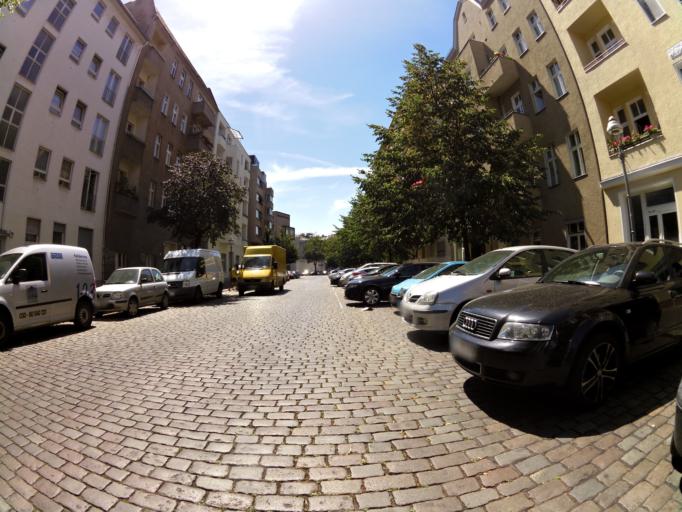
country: DE
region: Berlin
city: Wedding Bezirk
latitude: 52.5515
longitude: 13.3710
